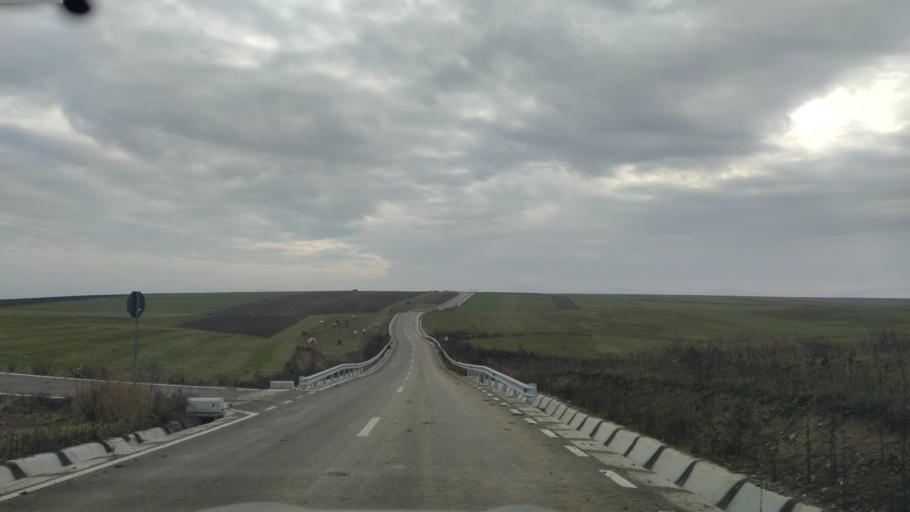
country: RO
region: Harghita
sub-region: Comuna Subcetate
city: Subcetate
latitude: 46.8220
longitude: 25.4468
